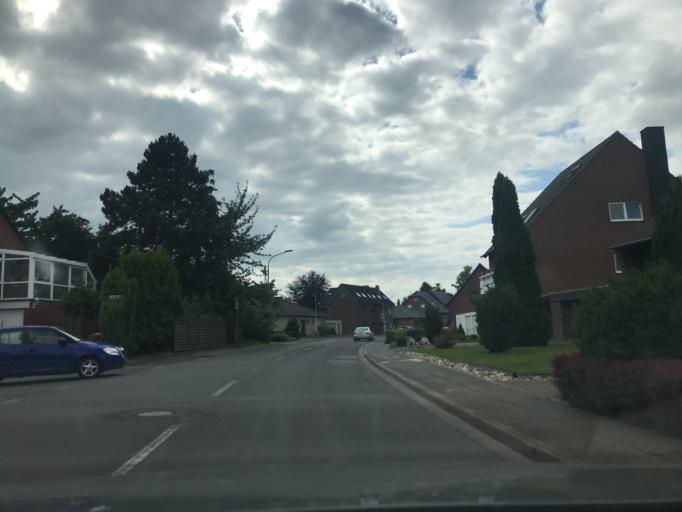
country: DE
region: North Rhine-Westphalia
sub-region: Regierungsbezirk Dusseldorf
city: Neuss
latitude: 51.1286
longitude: 6.7317
